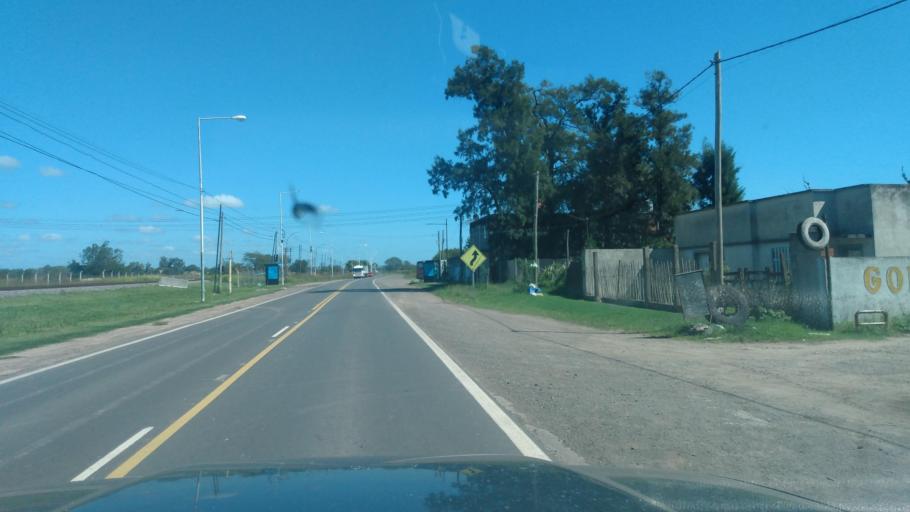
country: AR
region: Buenos Aires
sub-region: Partido de General Rodriguez
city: General Rodriguez
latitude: -34.5924
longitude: -59.0224
